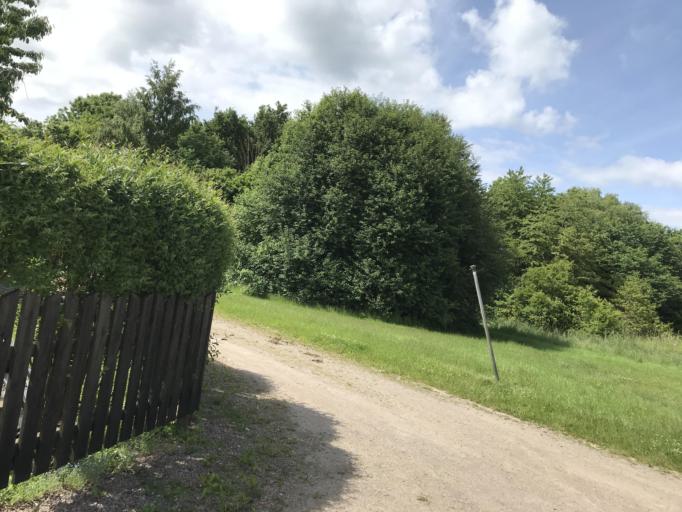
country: SE
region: Skane
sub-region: Landskrona
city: Landskrona
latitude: 55.8989
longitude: 12.8348
